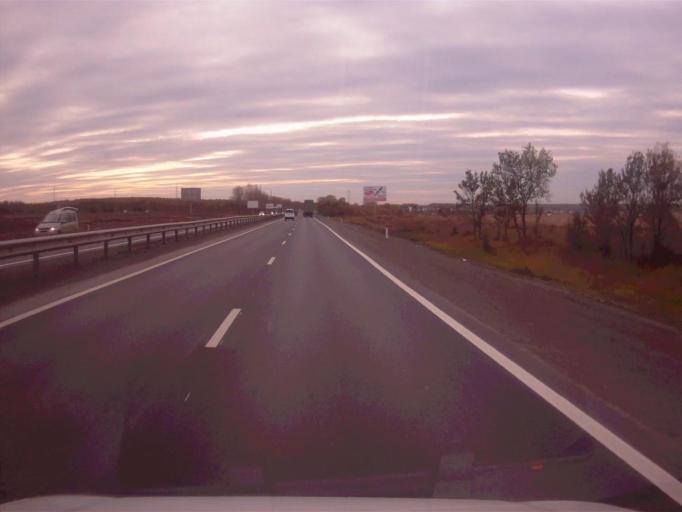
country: RU
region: Chelyabinsk
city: Roza
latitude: 54.9890
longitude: 61.4395
